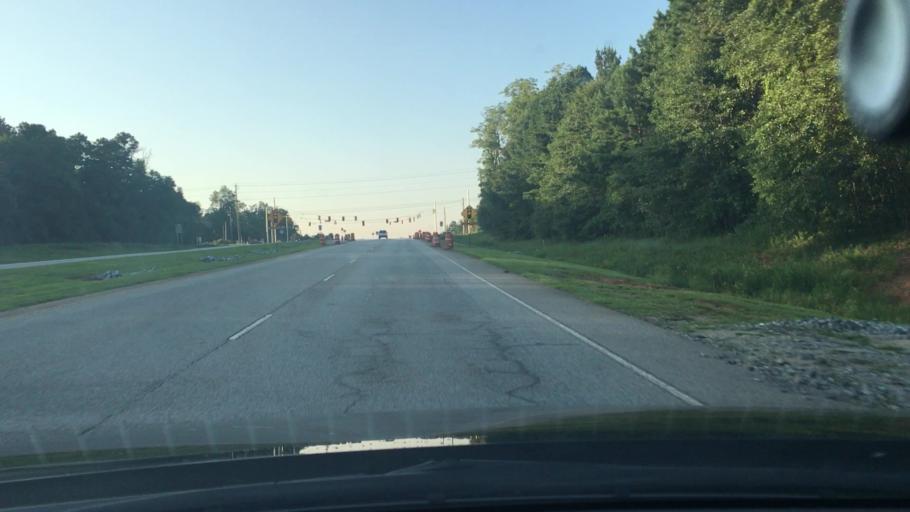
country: US
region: Georgia
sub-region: Coweta County
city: East Newnan
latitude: 33.3584
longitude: -84.7654
